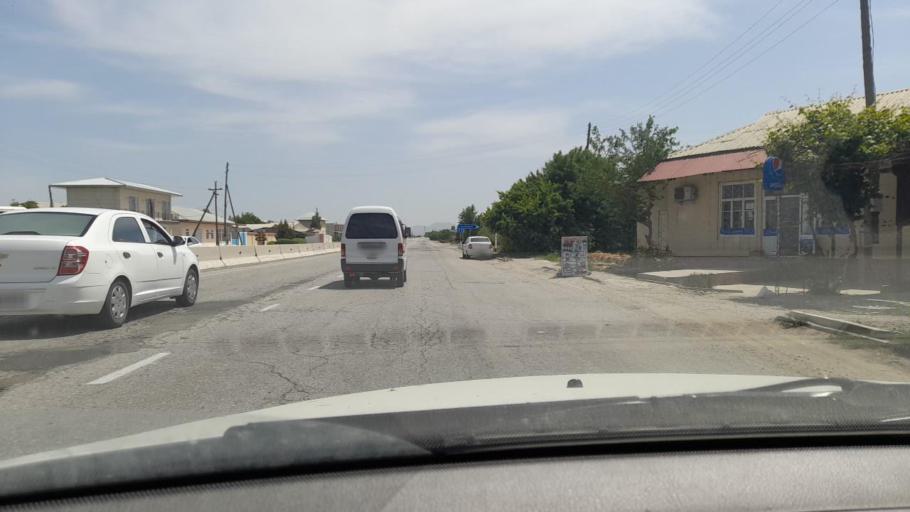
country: UZ
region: Navoiy
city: Karmana Shahri
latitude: 40.1377
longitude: 65.4016
